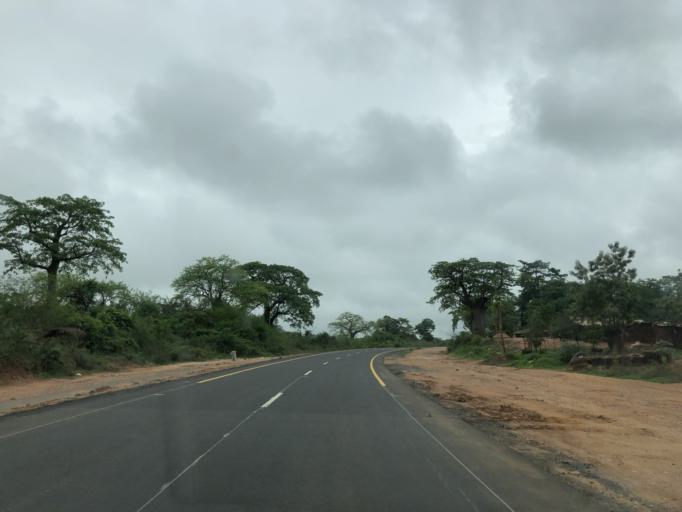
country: AO
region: Cuanza Norte
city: N'dalatando
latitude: -9.3916
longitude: 14.2888
